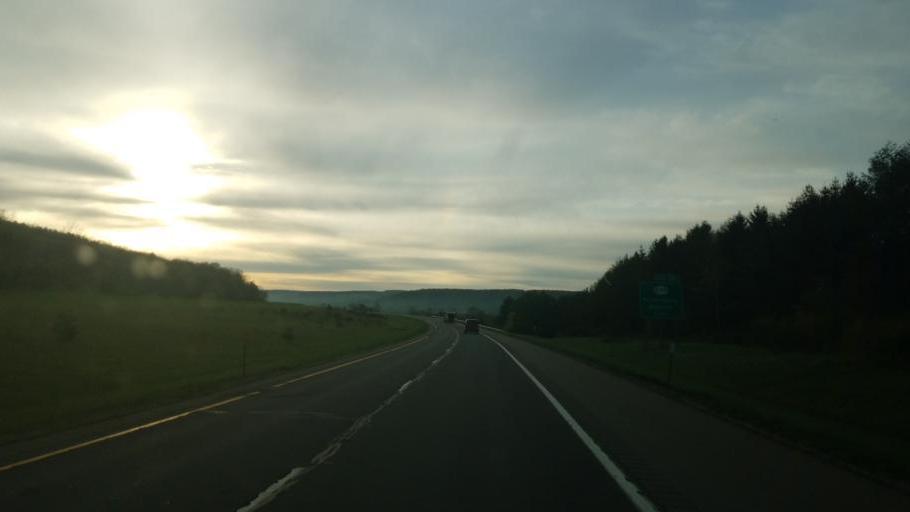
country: US
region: New York
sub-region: Allegany County
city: Friendship
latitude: 42.2025
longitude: -78.1707
